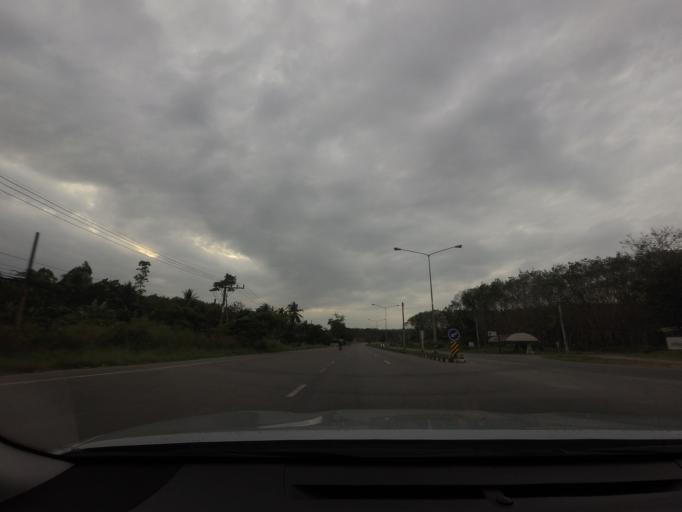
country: TH
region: Surat Thani
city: Phunphin
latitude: 9.0365
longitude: 99.1331
